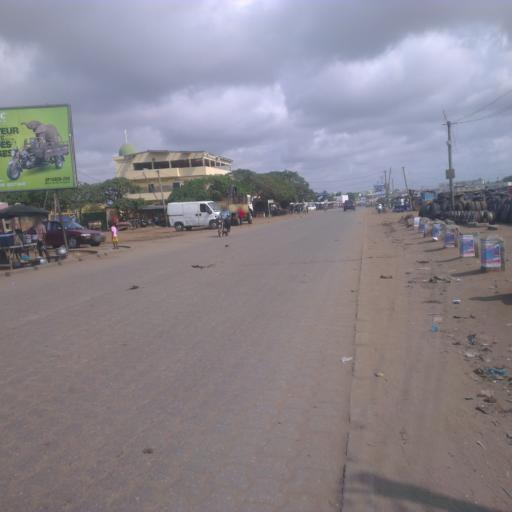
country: TG
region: Maritime
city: Lome
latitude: 6.1519
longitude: 1.2702
